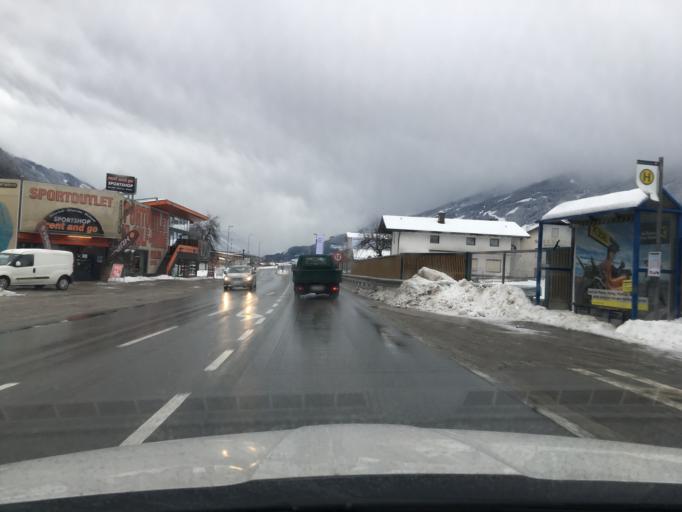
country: AT
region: Tyrol
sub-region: Politischer Bezirk Schwaz
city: Uderns
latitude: 47.3262
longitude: 11.8649
